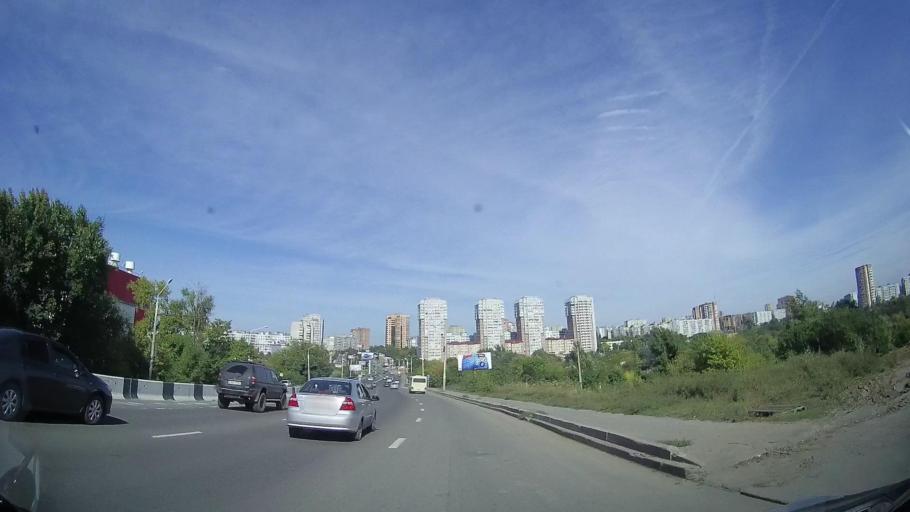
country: RU
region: Rostov
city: Severnyy
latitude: 47.2846
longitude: 39.6935
